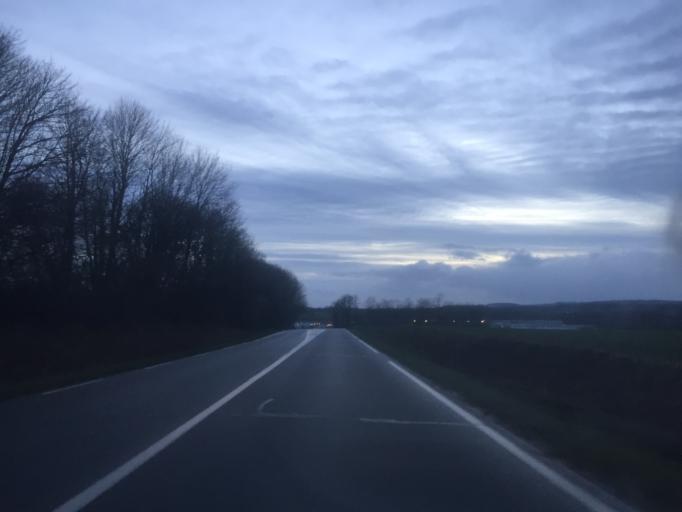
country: FR
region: Franche-Comte
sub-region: Departement du Jura
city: Dole
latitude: 47.1340
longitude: 5.5685
